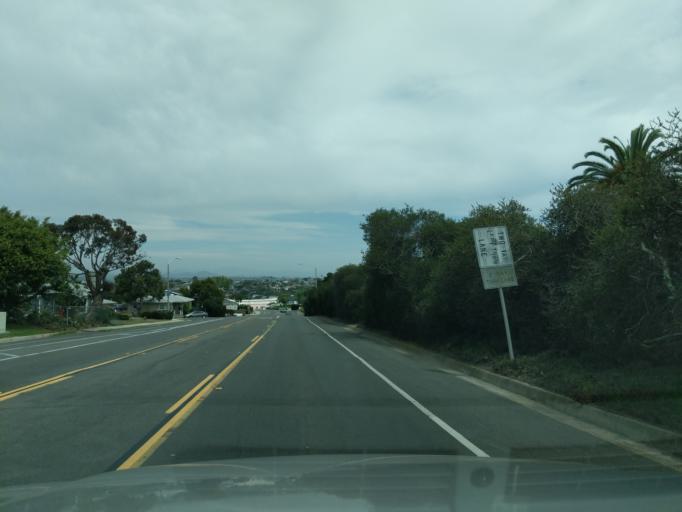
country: US
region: California
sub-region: San Diego County
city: Coronado
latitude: 32.7321
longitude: -117.2373
